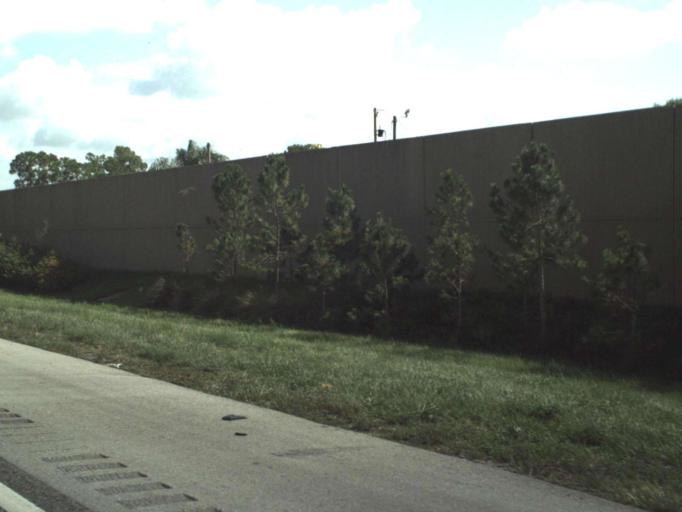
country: US
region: Florida
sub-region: Palm Beach County
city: Limestone Creek
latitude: 26.8956
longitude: -80.1352
